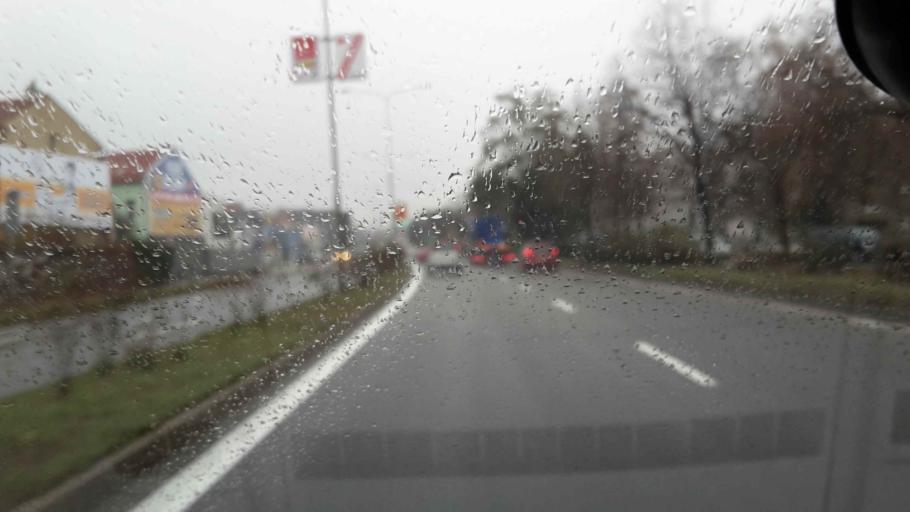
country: CZ
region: South Moravian
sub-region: Mesto Brno
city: Brno
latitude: 49.1937
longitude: 16.6469
